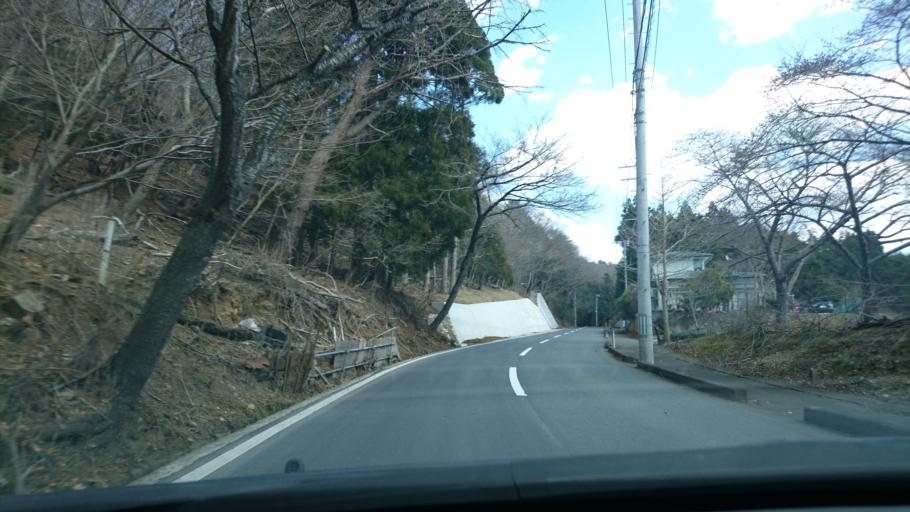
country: JP
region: Miyagi
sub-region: Oshika Gun
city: Onagawa Cho
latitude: 38.4699
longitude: 141.4722
